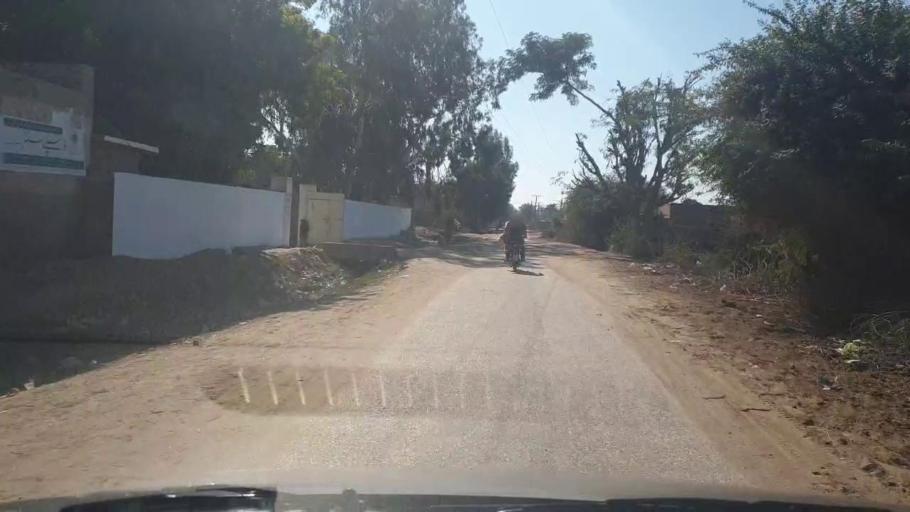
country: PK
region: Sindh
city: Bozdar
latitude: 27.0935
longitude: 68.6250
